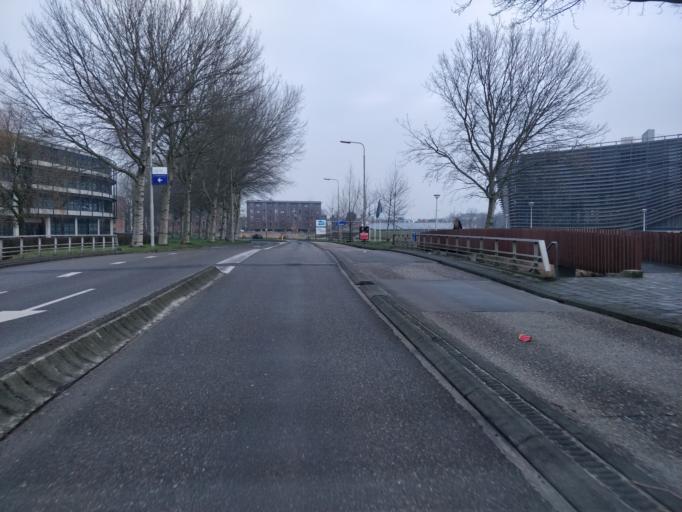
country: NL
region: Friesland
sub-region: Gemeente Leeuwarden
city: Leeuwarden
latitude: 53.1954
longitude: 5.8021
